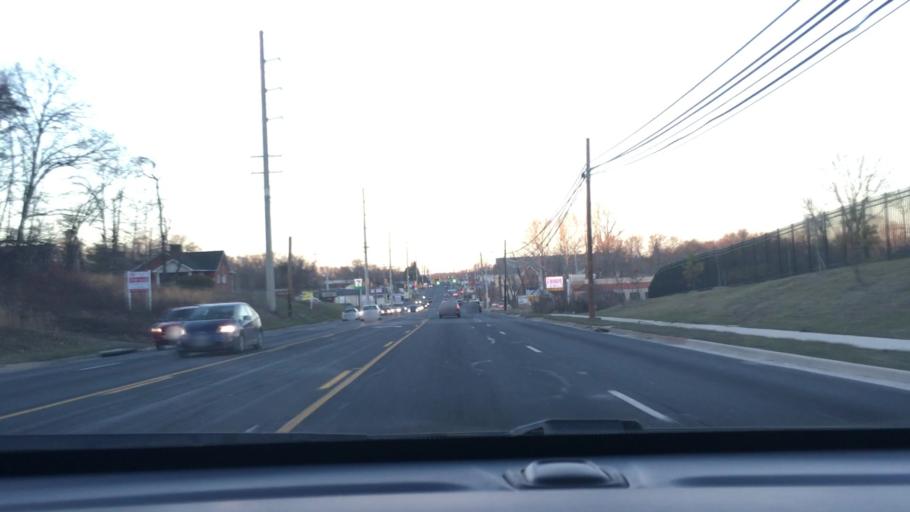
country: US
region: Virginia
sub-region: Prince William County
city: Yorkshire
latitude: 38.7853
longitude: -77.4494
